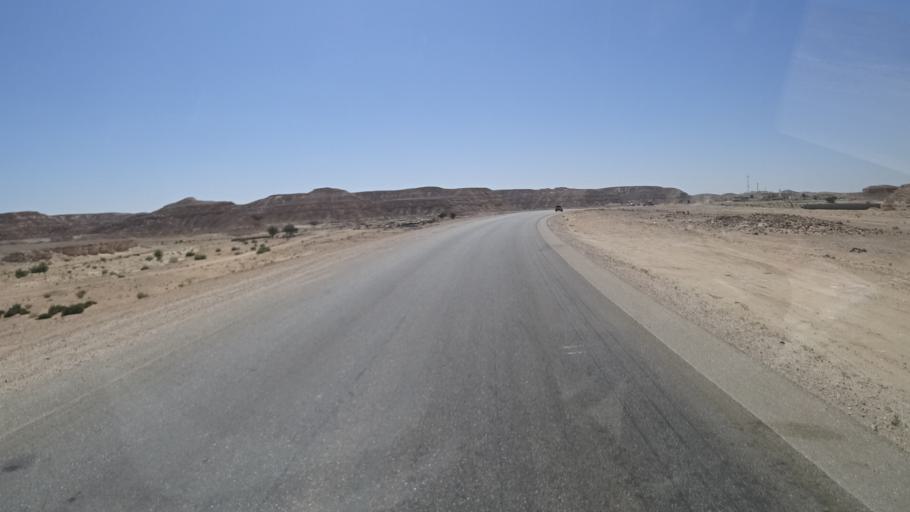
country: OM
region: Zufar
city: Salalah
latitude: 17.4918
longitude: 53.3604
